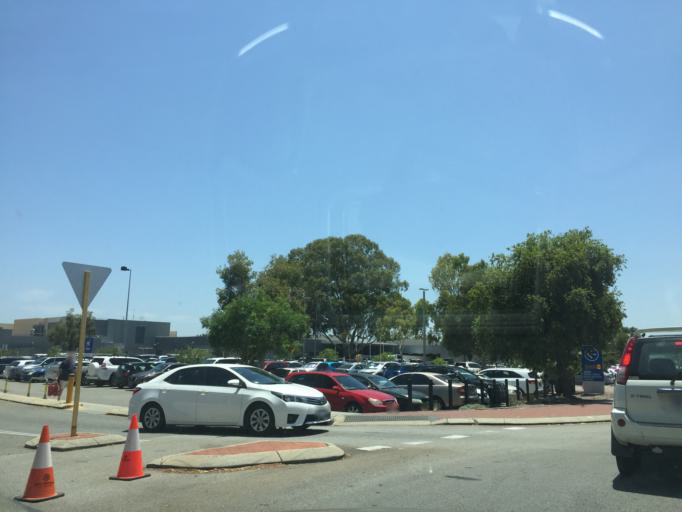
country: AU
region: Western Australia
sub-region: Canning
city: Cannington
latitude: -32.0194
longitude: 115.9390
